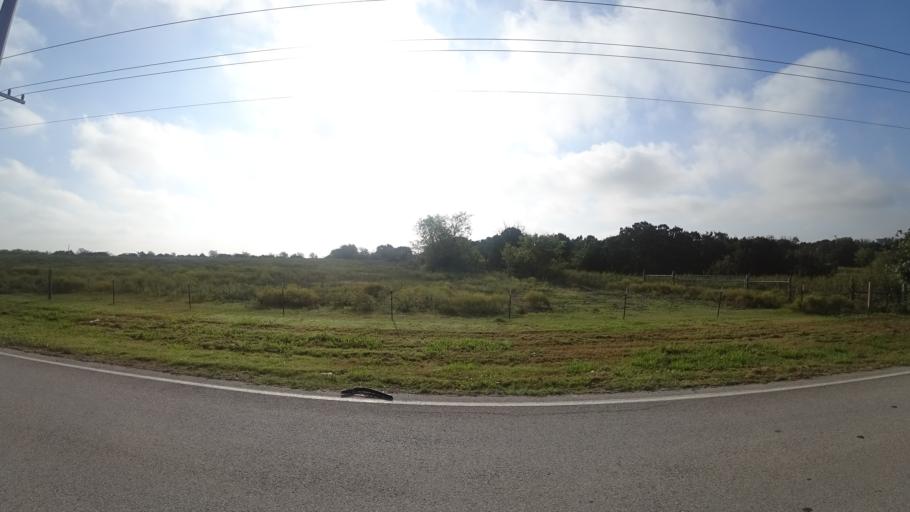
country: US
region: Texas
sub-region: Travis County
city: Manor
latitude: 30.3566
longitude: -97.6346
